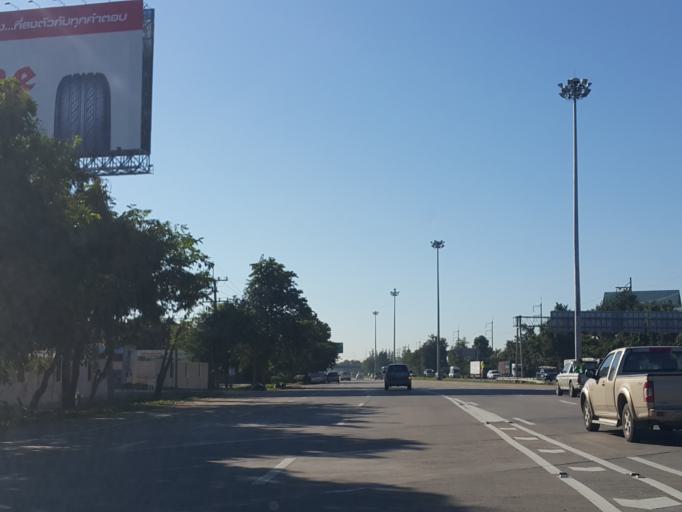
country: TH
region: Chiang Mai
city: Saraphi
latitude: 18.7597
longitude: 99.0303
